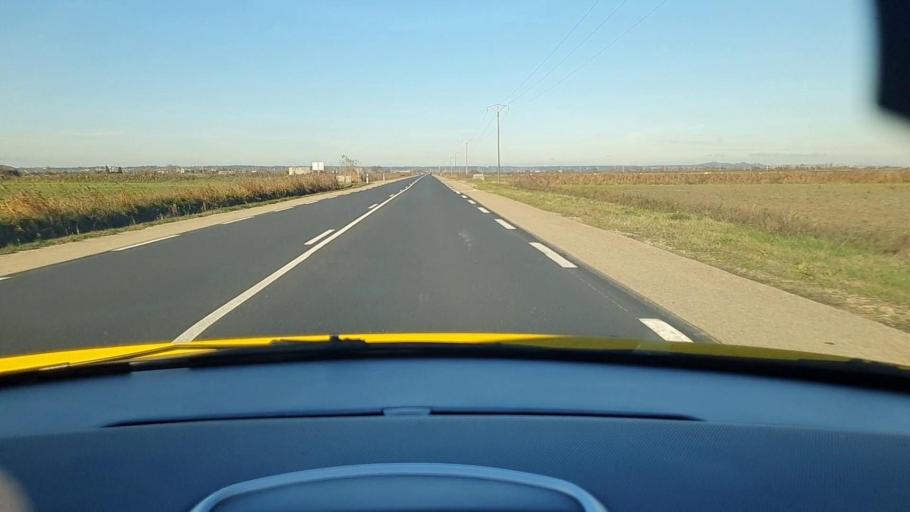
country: FR
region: Languedoc-Roussillon
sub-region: Departement du Gard
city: Bellegarde
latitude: 43.7143
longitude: 4.5487
